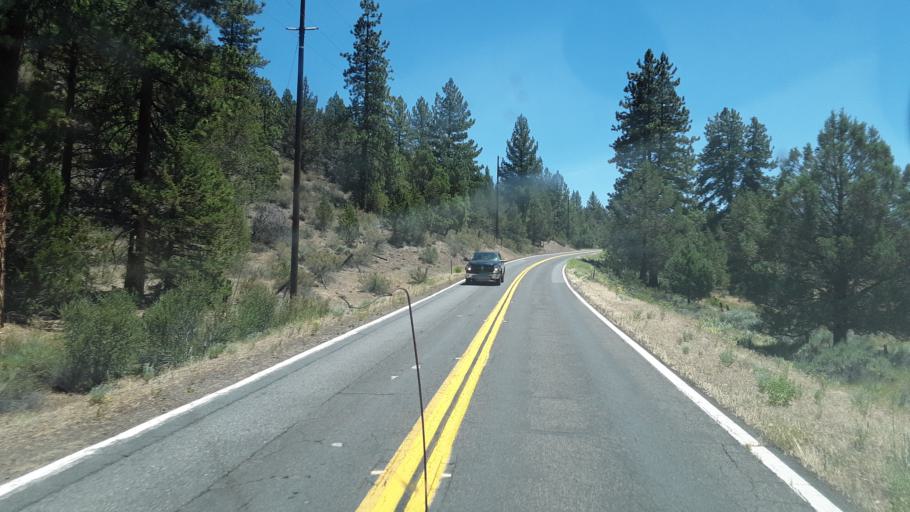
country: US
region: California
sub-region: Modoc County
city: Alturas
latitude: 41.0754
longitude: -120.8902
